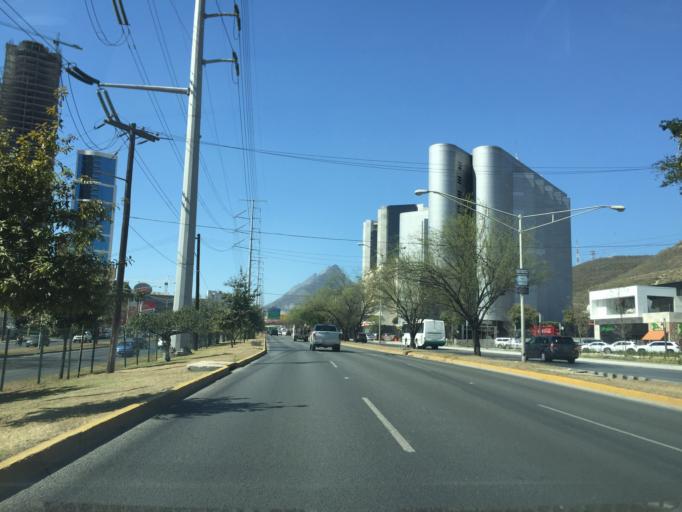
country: MX
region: Nuevo Leon
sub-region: Monterrey
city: Monterrey
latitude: 25.6492
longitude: -100.3292
